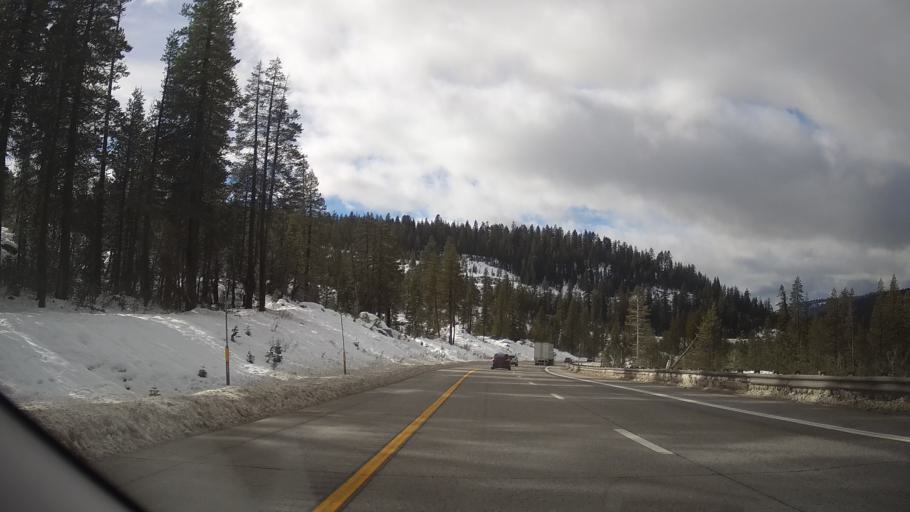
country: US
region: California
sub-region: Nevada County
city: Truckee
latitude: 39.3233
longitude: -120.4020
